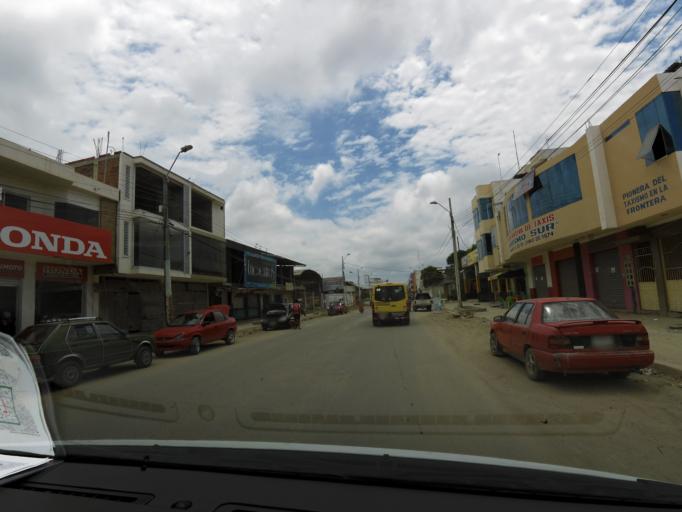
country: EC
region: El Oro
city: Huaquillas
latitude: -3.4821
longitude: -80.2323
